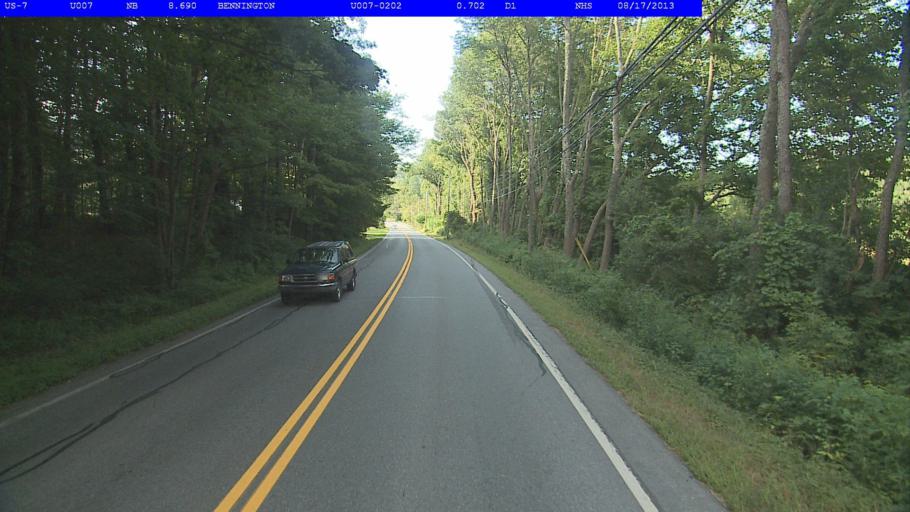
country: US
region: Vermont
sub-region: Bennington County
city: Bennington
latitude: 42.8474
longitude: -73.2021
